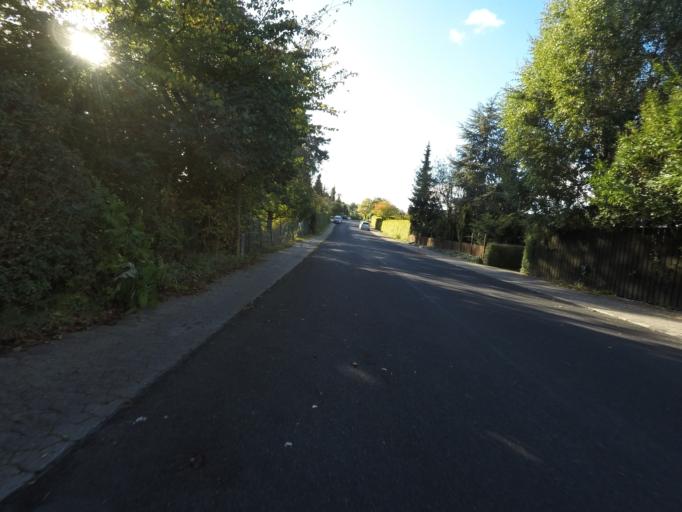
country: DK
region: Capital Region
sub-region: Ballerup Kommune
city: Ballerup
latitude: 55.7472
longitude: 12.3876
